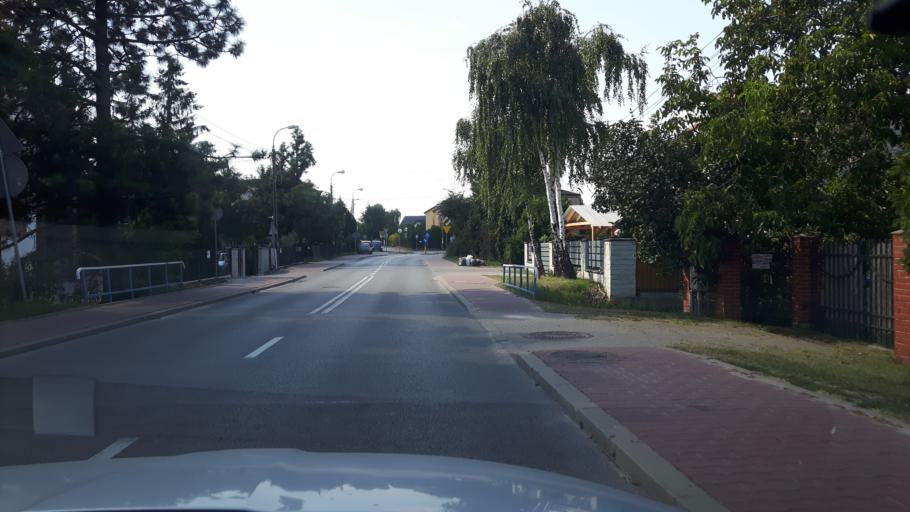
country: PL
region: Masovian Voivodeship
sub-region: Powiat pruszkowski
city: Nowe Grocholice
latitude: 52.1603
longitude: 20.9164
